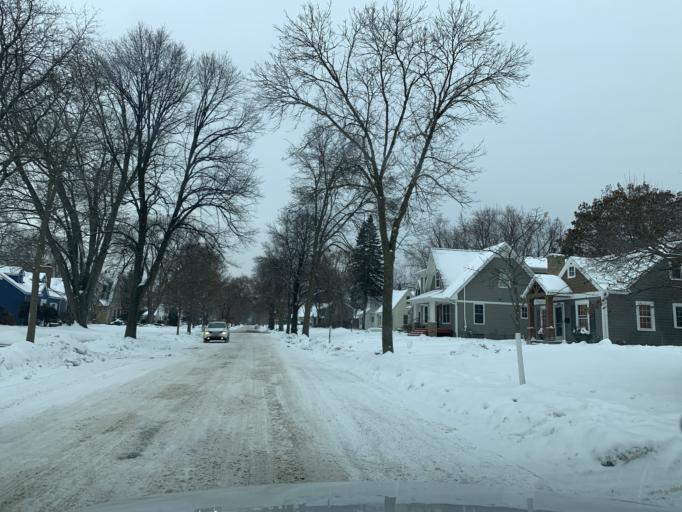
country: US
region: Minnesota
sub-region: Hennepin County
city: Saint Louis Park
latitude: 44.9352
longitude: -93.3341
